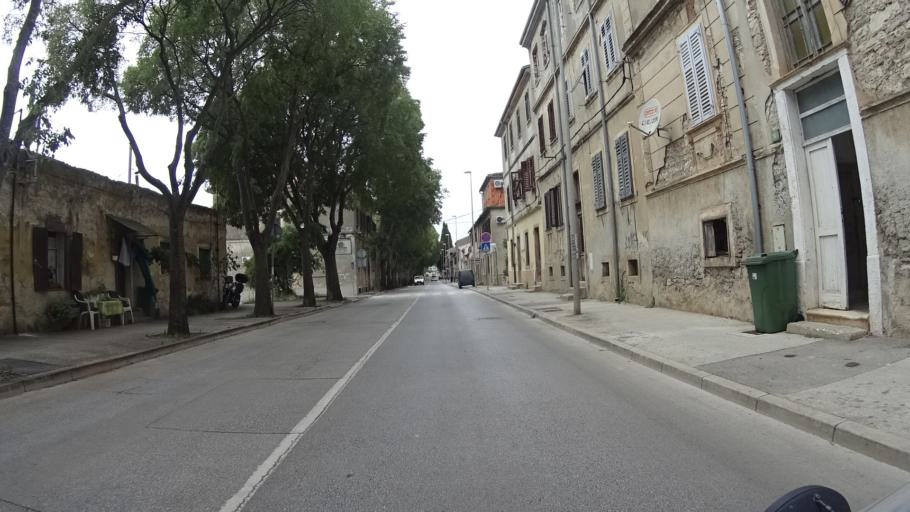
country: HR
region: Istarska
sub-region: Grad Pula
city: Pula
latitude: 44.8635
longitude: 13.8571
